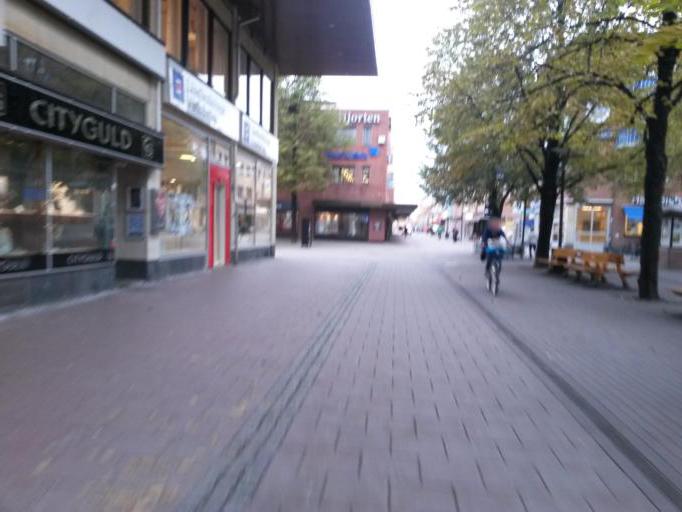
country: SE
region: Vaesterbotten
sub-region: Skelleftea Kommun
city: Skelleftea
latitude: 64.7507
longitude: 20.9538
